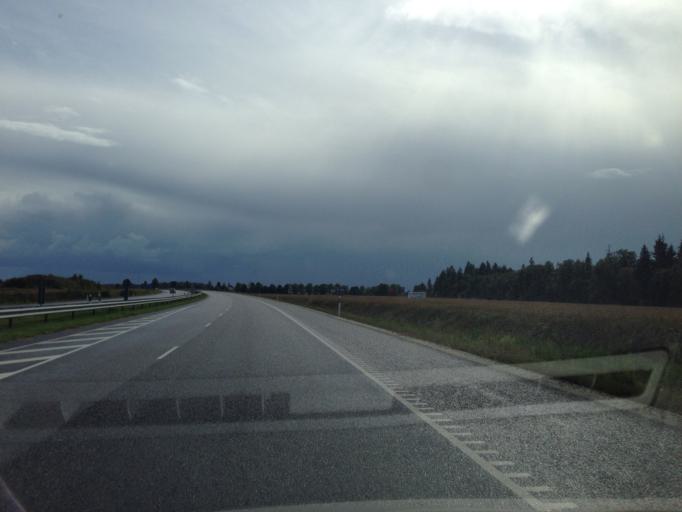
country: EE
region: Jaervamaa
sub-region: Paide linn
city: Paide
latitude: 58.9360
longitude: 25.6101
